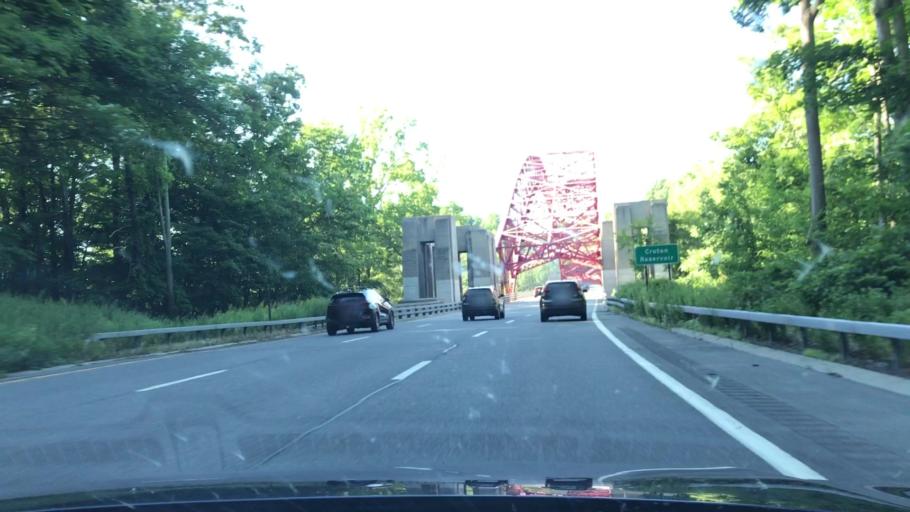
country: US
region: New York
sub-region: Westchester County
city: Yorktown Heights
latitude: 41.2356
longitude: -73.8127
